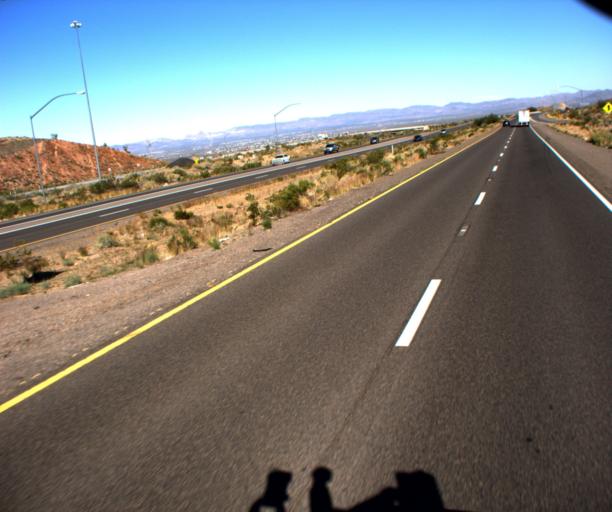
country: US
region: Arizona
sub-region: Mohave County
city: Kingman
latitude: 35.2194
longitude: -114.1214
